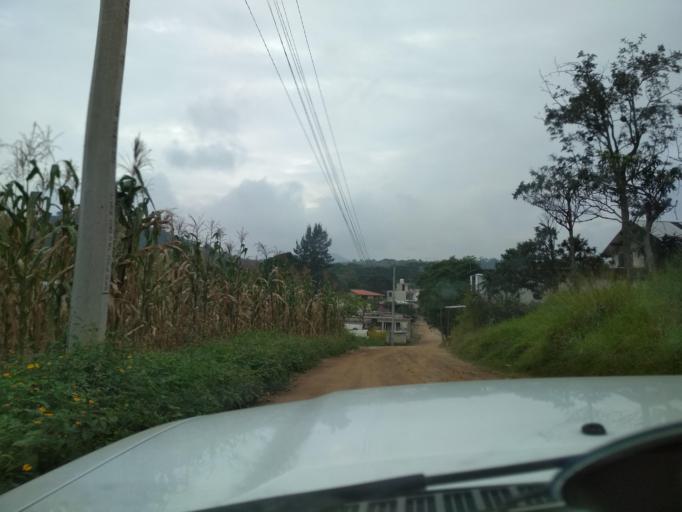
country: MX
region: Veracruz
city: El Castillo
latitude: 19.5632
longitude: -96.8581
